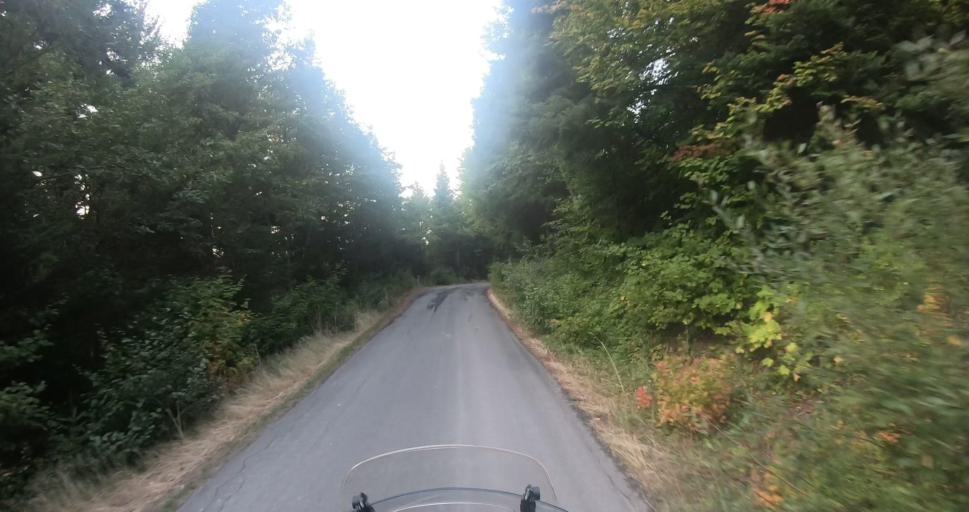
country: US
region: Oregon
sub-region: Hood River County
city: Odell
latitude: 45.4603
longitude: -121.6288
